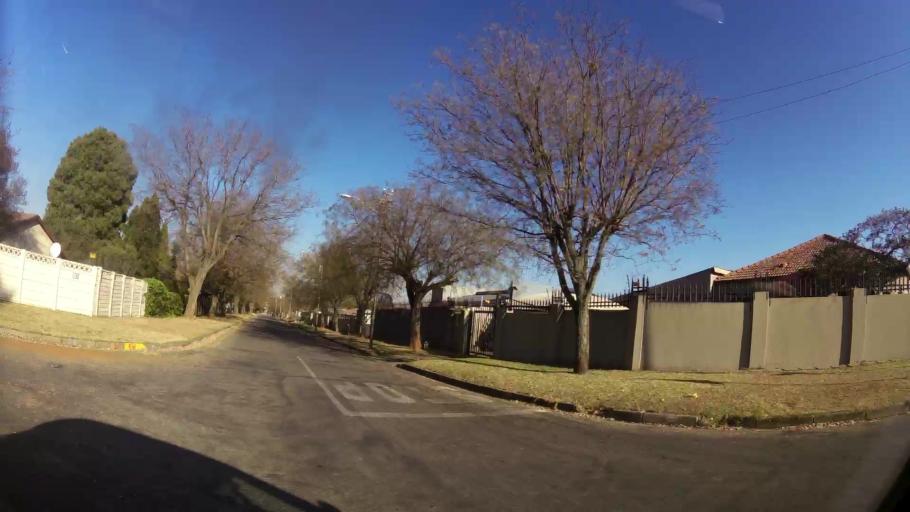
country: ZA
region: Gauteng
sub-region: Ekurhuleni Metropolitan Municipality
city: Germiston
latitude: -26.1964
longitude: 28.1362
